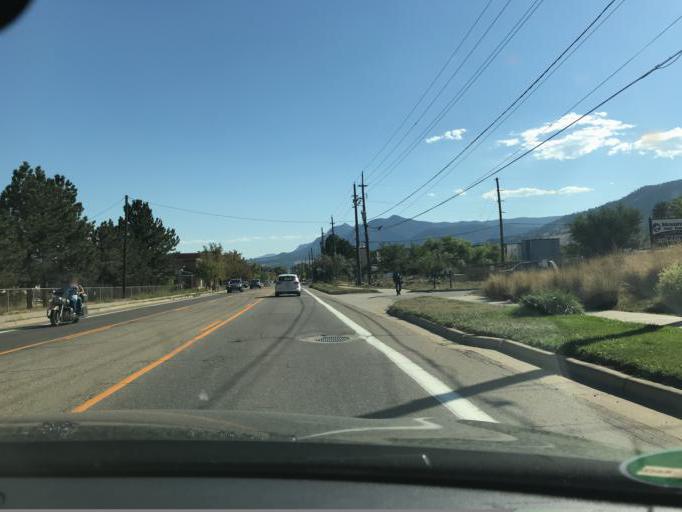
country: US
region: Colorado
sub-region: Boulder County
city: Boulder
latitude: 40.0609
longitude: -105.2823
